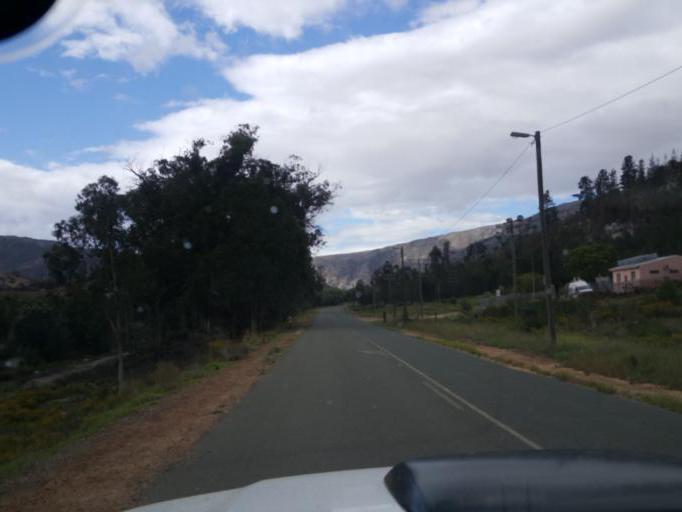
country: ZA
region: Western Cape
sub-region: Eden District Municipality
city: George
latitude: -33.8414
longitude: 22.4438
